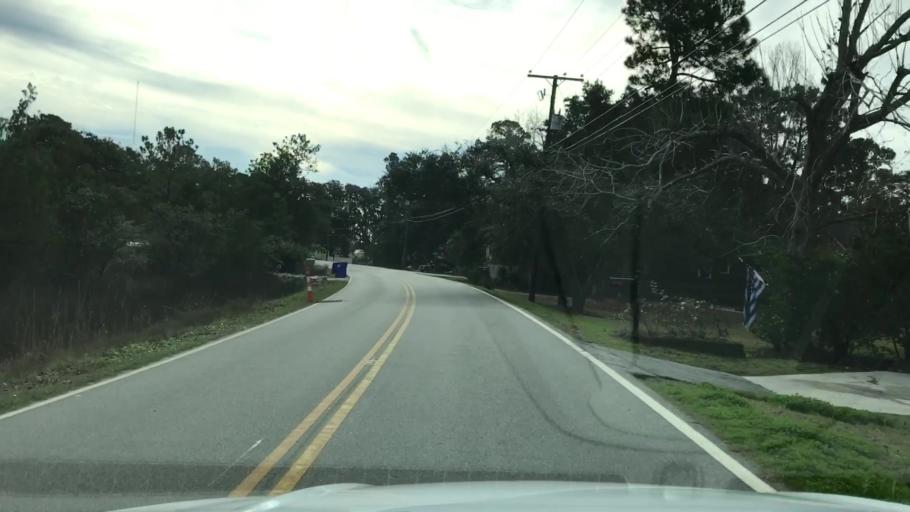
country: US
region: South Carolina
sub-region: Charleston County
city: Charleston
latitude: 32.7769
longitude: -80.0189
